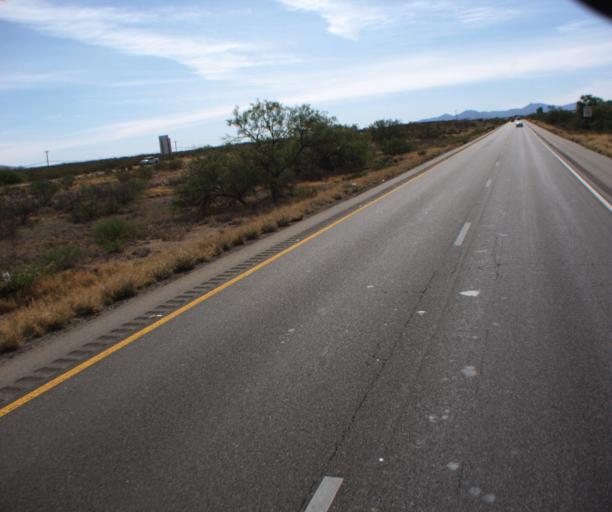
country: US
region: Arizona
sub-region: Pima County
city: Vail
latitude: 32.0211
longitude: -110.7118
